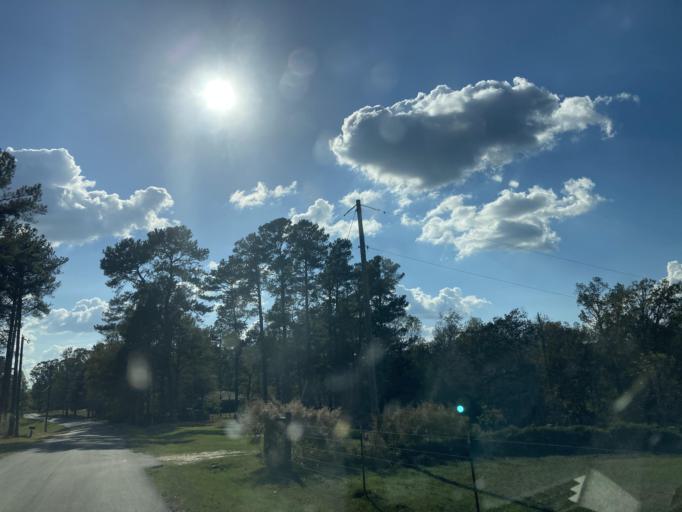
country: US
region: Mississippi
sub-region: Lamar County
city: Sumrall
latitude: 31.4161
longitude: -89.6248
